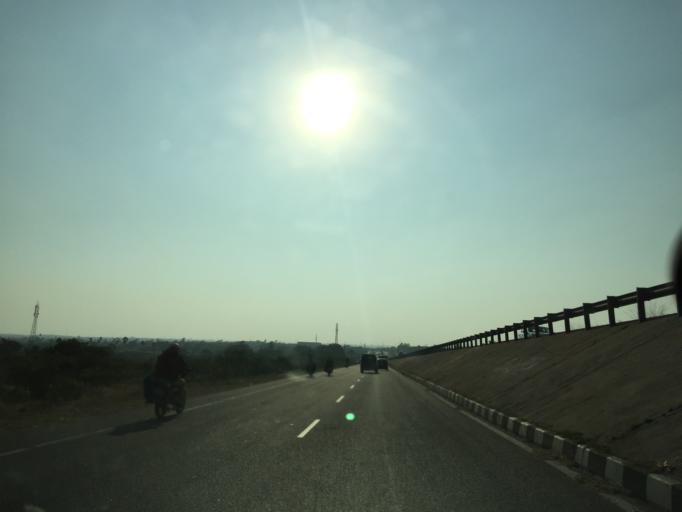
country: IN
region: Telangana
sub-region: Nalgonda
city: Gudur
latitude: 17.5017
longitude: 78.8488
